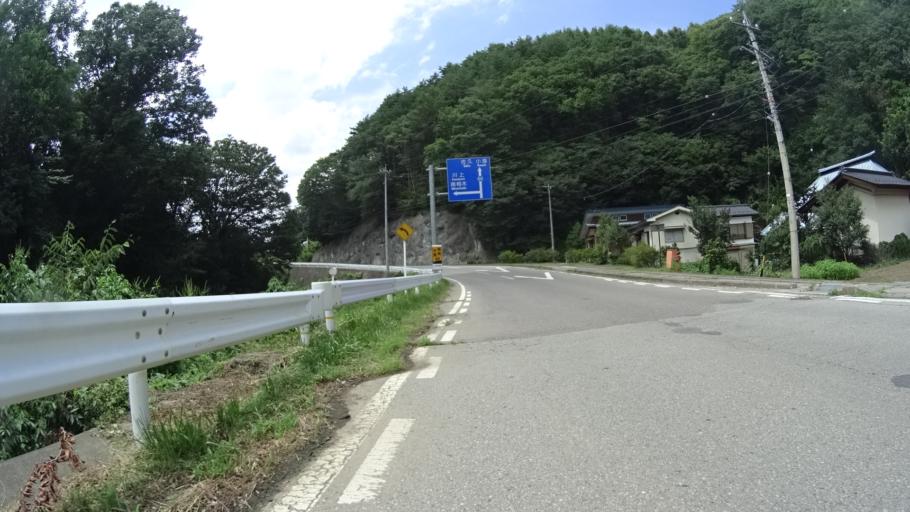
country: JP
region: Nagano
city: Saku
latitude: 36.0594
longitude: 138.5458
